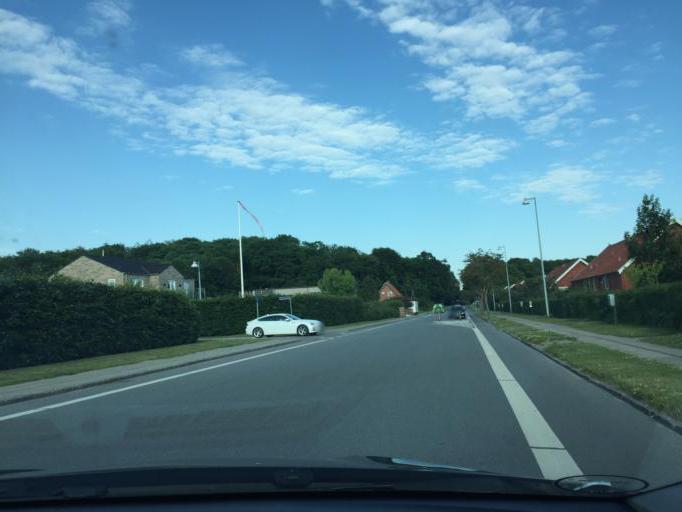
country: DK
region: South Denmark
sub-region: Odense Kommune
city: Stige
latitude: 55.4175
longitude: 10.4067
